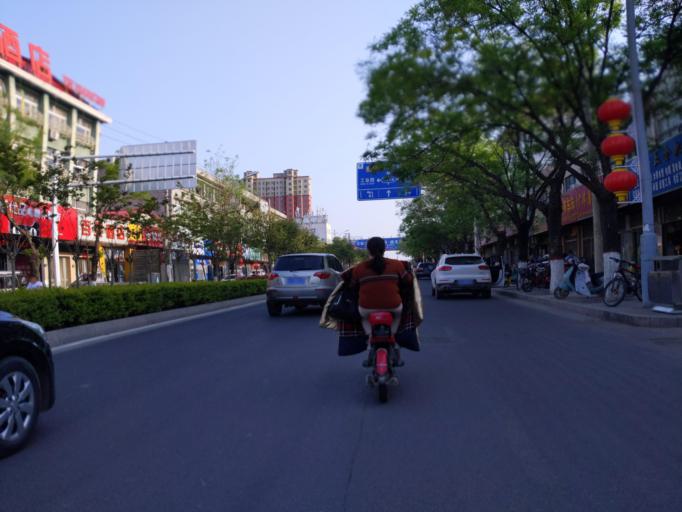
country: CN
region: Henan Sheng
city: Puyang Chengguanzhen
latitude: 35.7003
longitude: 115.0162
